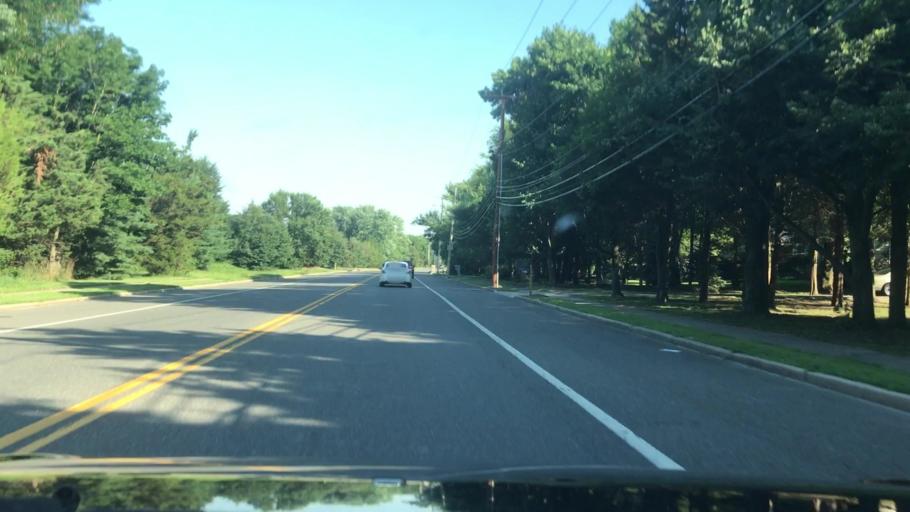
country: US
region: New Jersey
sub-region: Ocean County
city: Silver Ridge
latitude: 39.9991
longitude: -74.1992
